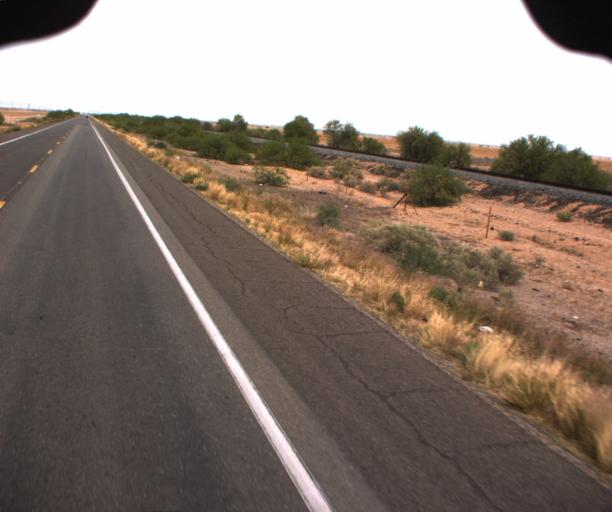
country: US
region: Arizona
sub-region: Pinal County
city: Sacaton
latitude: 33.1560
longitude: -111.7762
